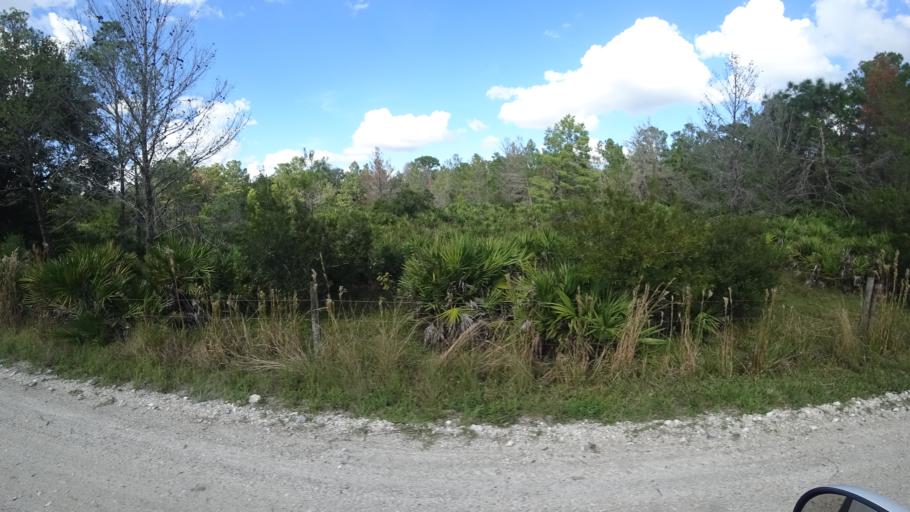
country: US
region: Florida
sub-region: Hillsborough County
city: Wimauma
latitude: 27.4374
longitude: -82.1497
